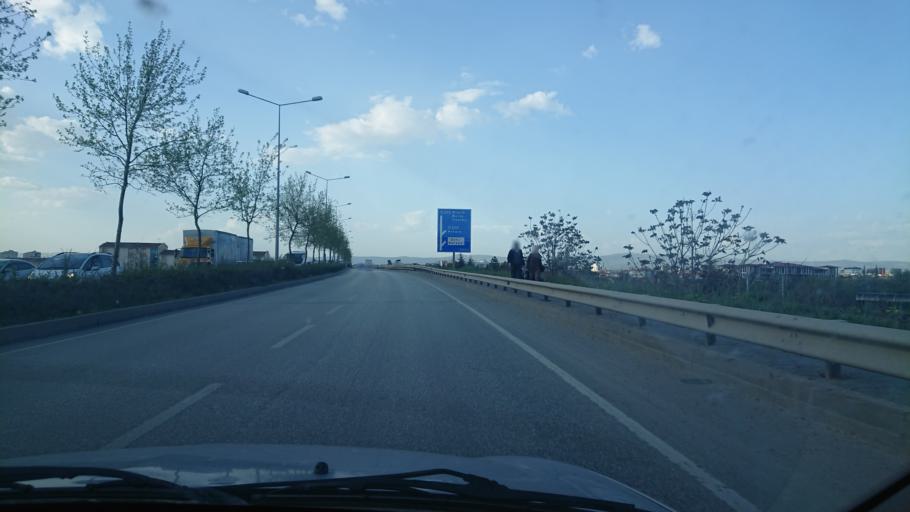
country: TR
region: Eskisehir
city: Eskisehir
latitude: 39.7731
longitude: 30.4838
